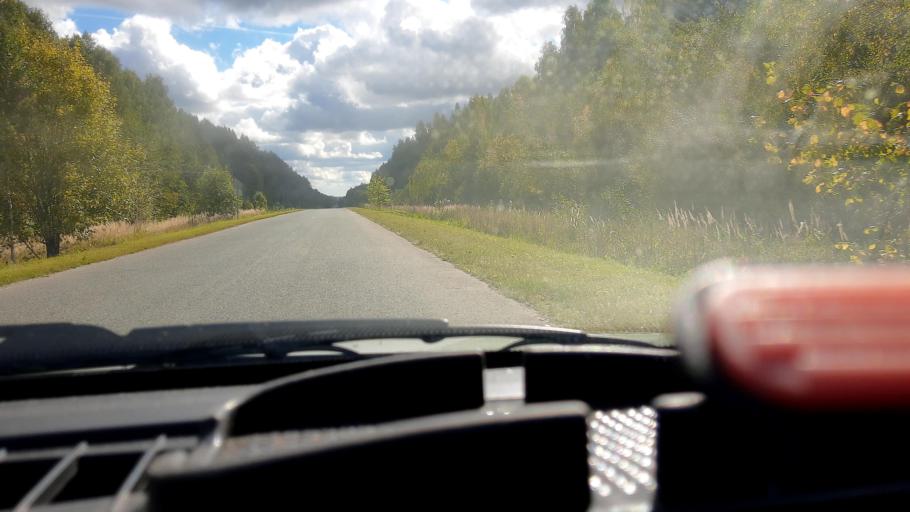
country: RU
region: Mariy-El
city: Kilemary
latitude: 56.9229
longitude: 46.7127
